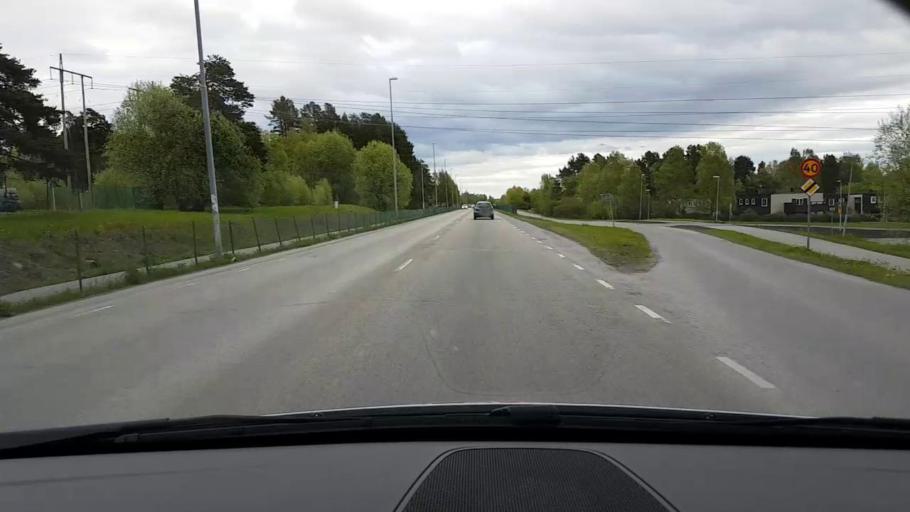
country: SE
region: Jaemtland
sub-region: OEstersunds Kommun
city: Ostersund
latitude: 63.1584
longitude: 14.6727
